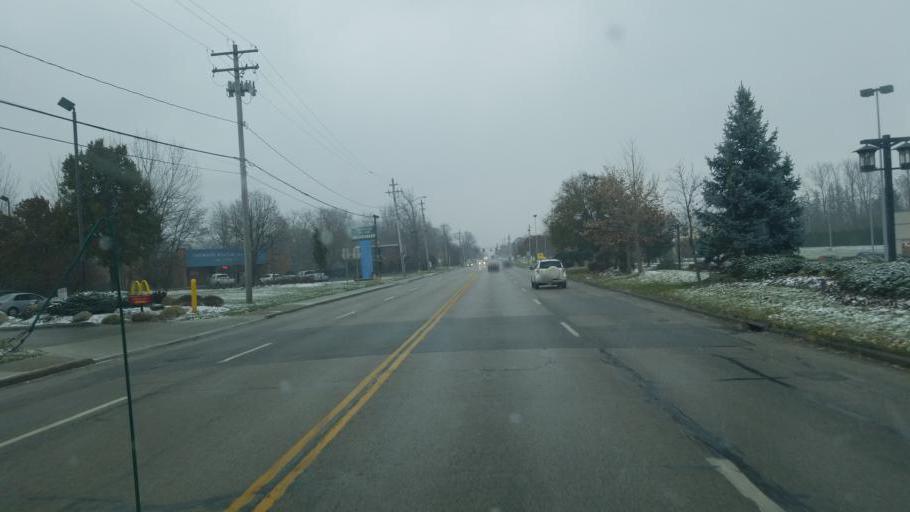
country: US
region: Ohio
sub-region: Cuyahoga County
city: Oakwood
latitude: 41.3676
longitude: -81.5110
